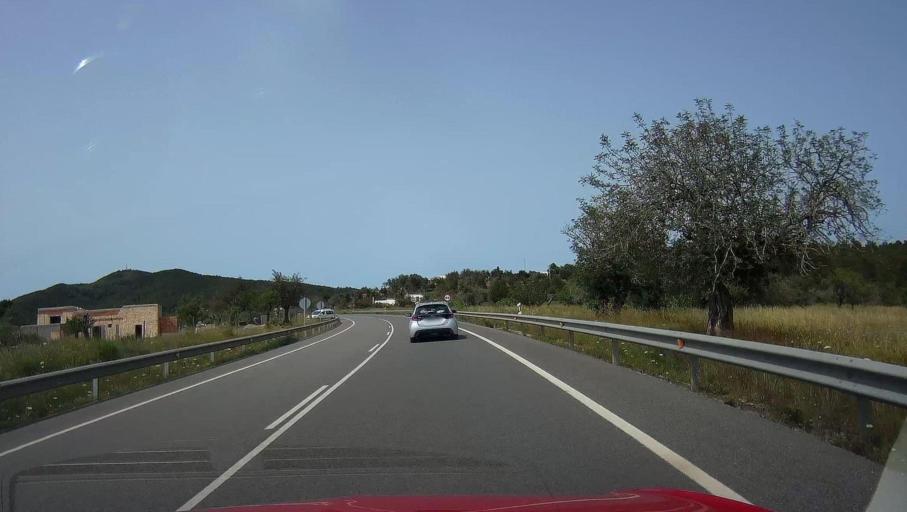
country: ES
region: Balearic Islands
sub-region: Illes Balears
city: Sant Joan de Labritja
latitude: 39.0613
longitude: 1.4951
